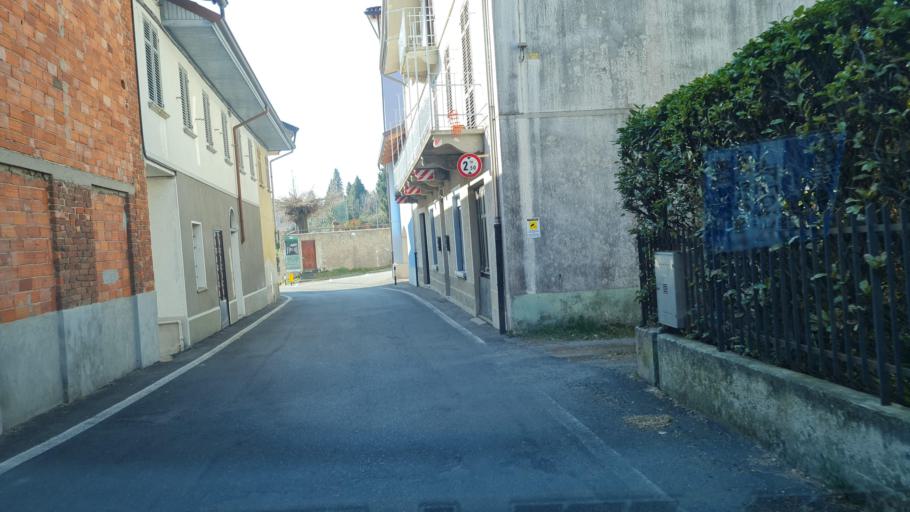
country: IT
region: Piedmont
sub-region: Provincia di Biella
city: Bioglio-Portula-Andre
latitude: 45.6136
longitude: 8.1297
